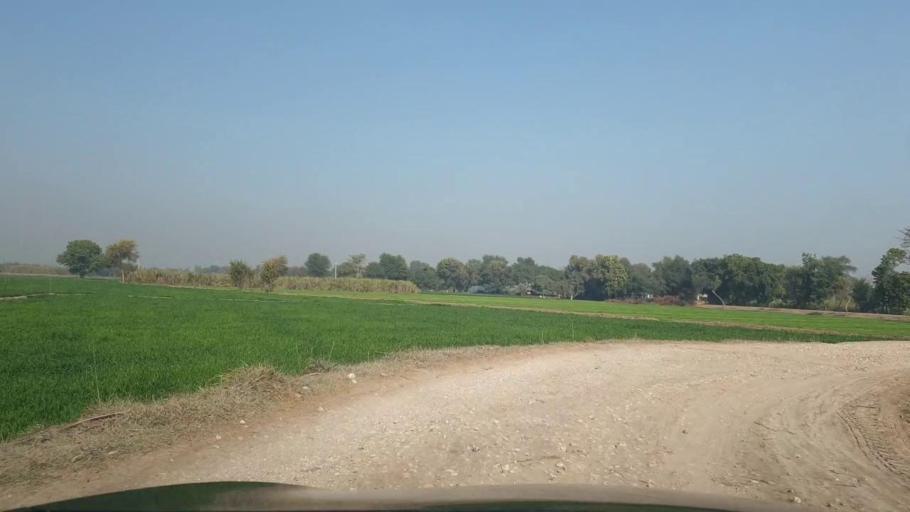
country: PK
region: Sindh
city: Ubauro
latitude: 28.1138
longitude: 69.7479
